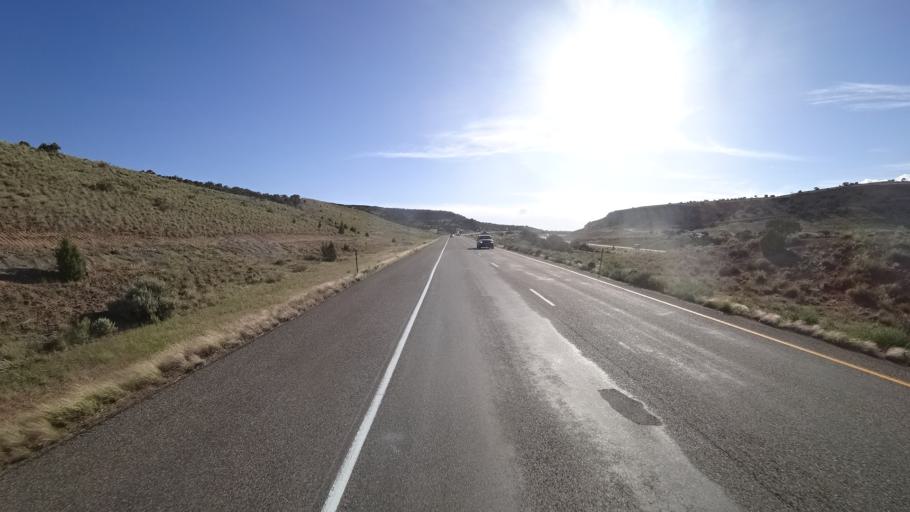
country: US
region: Colorado
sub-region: Mesa County
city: Loma
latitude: 39.1887
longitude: -109.0271
